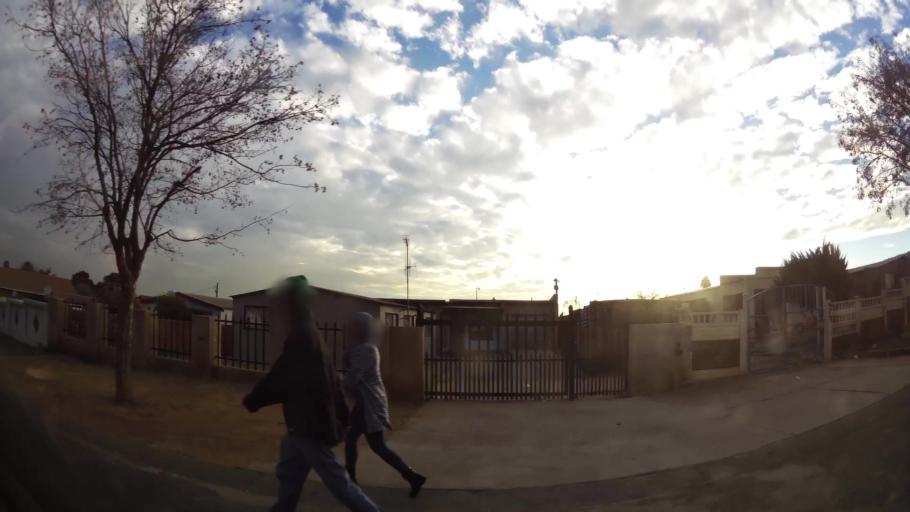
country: ZA
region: Gauteng
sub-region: City of Tshwane Metropolitan Municipality
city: Pretoria
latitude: -25.7035
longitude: 28.3179
